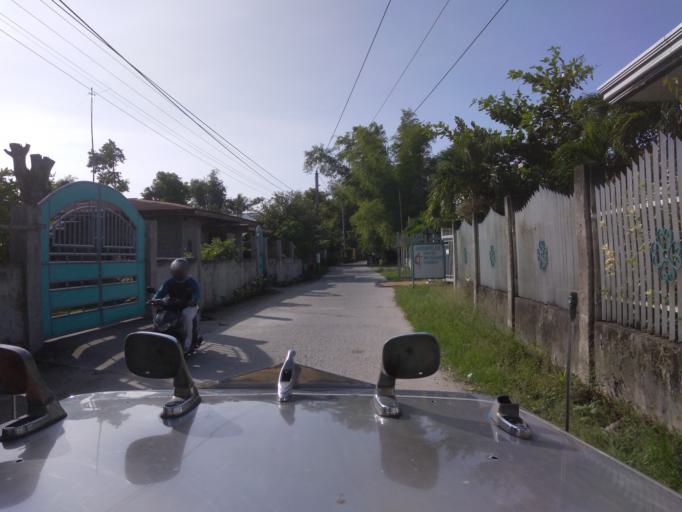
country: PH
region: Central Luzon
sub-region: Province of Pampanga
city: Bulaon
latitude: 15.0929
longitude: 120.6950
